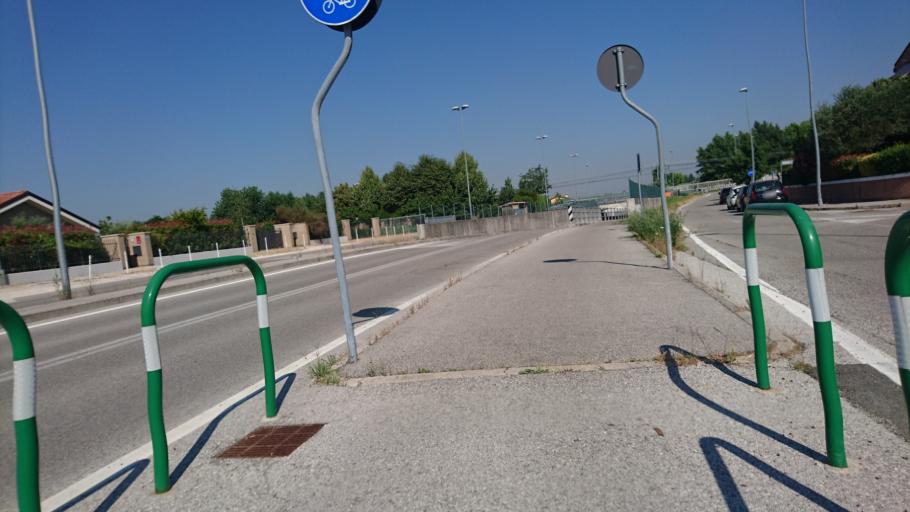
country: IT
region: Veneto
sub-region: Provincia di Padova
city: Mandriola-Sant'Agostino
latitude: 45.3693
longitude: 11.8236
